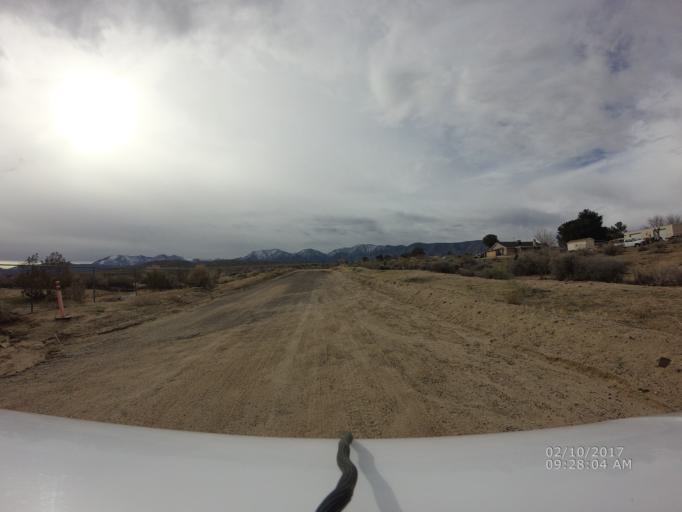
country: US
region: California
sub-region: Los Angeles County
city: Littlerock
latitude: 34.4947
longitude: -117.8900
